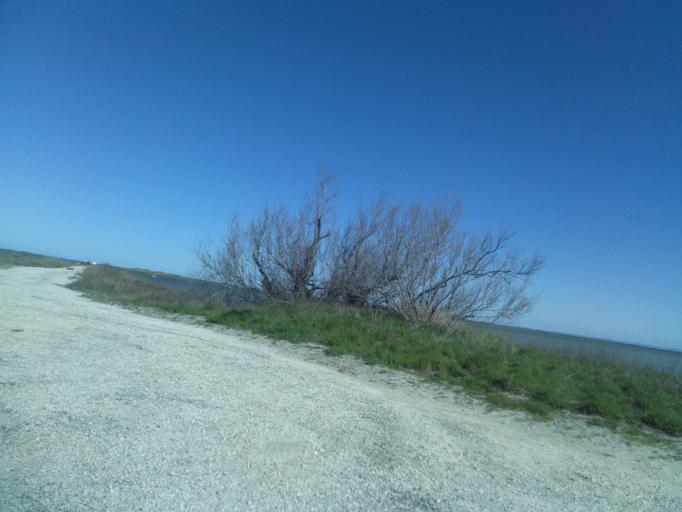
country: FR
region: Provence-Alpes-Cote d'Azur
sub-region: Departement des Bouches-du-Rhone
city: Saintes-Maries-de-la-Mer
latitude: 43.4150
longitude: 4.6139
